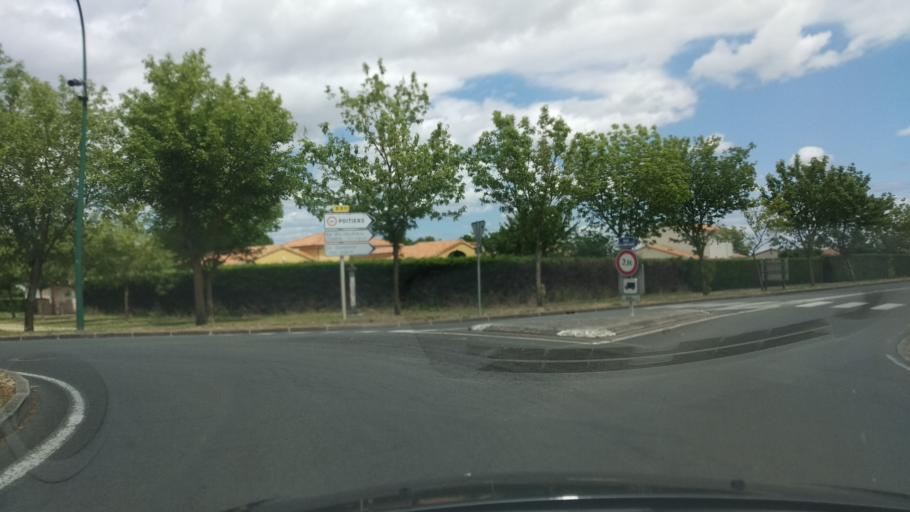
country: FR
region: Poitou-Charentes
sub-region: Departement de la Vienne
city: Vouneuil-sous-Biard
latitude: 46.5680
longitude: 0.2722
